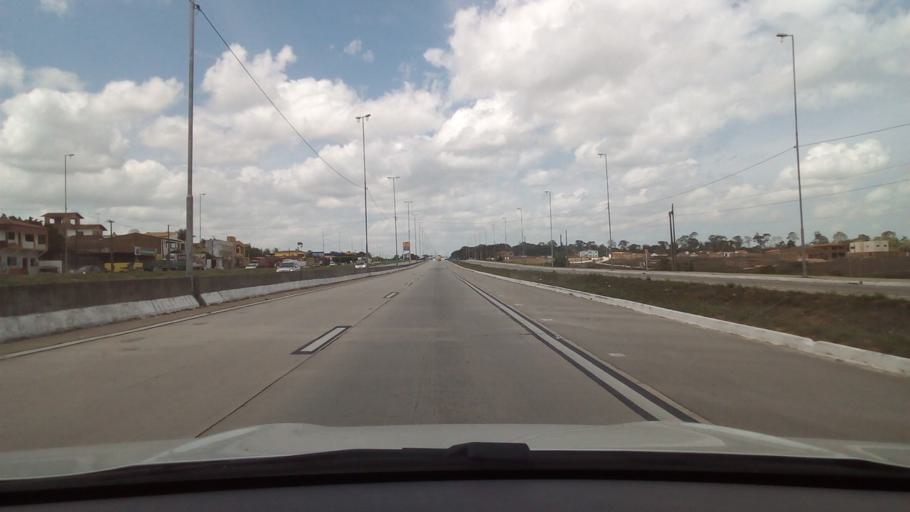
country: BR
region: Paraiba
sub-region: Mamanguape
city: Mamanguape
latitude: -6.8319
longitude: -35.1372
